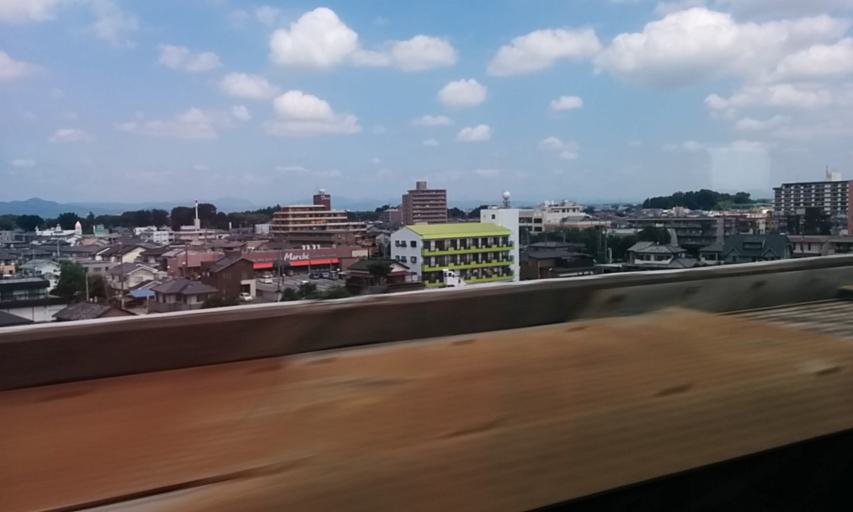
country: JP
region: Tochigi
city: Oyama
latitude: 36.3029
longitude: 139.7996
